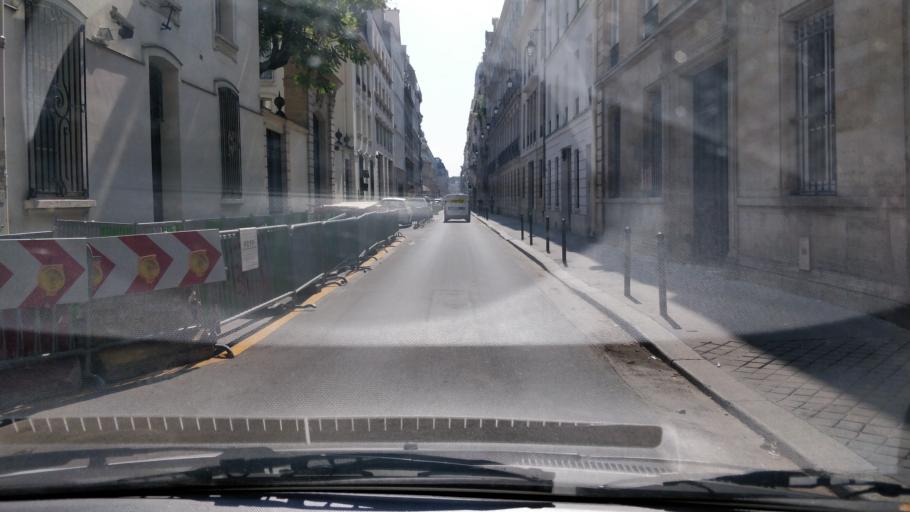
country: FR
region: Ile-de-France
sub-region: Paris
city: Paris
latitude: 48.8608
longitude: 2.3219
